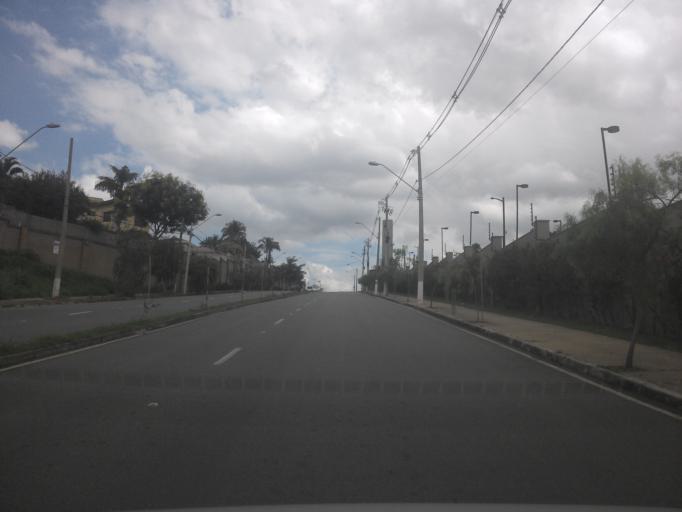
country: BR
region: Sao Paulo
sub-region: Campinas
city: Campinas
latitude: -22.8650
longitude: -47.0284
